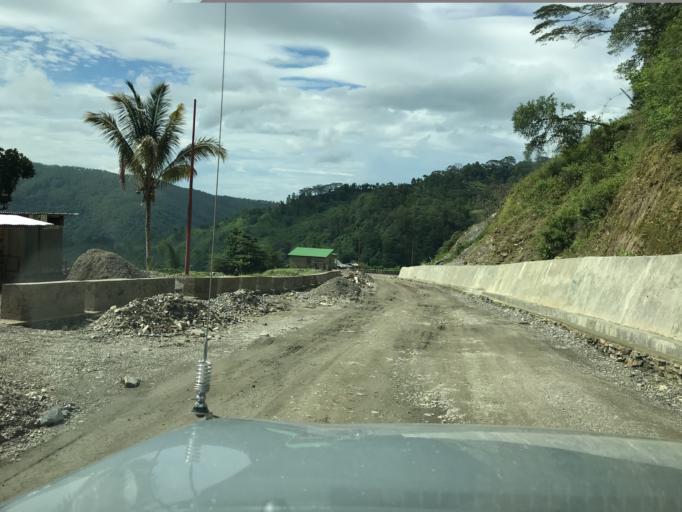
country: TL
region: Aileu
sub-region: Aileu Villa
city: Aileu
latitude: -8.6515
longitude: 125.5269
